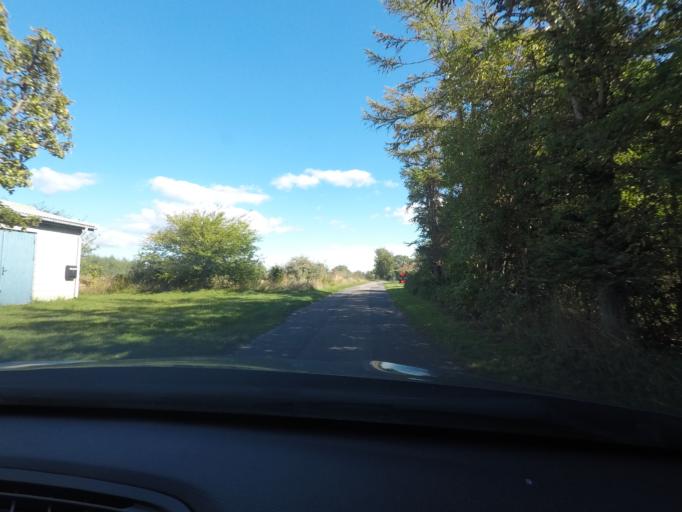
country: DK
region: Zealand
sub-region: Guldborgsund Kommune
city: Sakskobing
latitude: 54.9740
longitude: 11.5586
